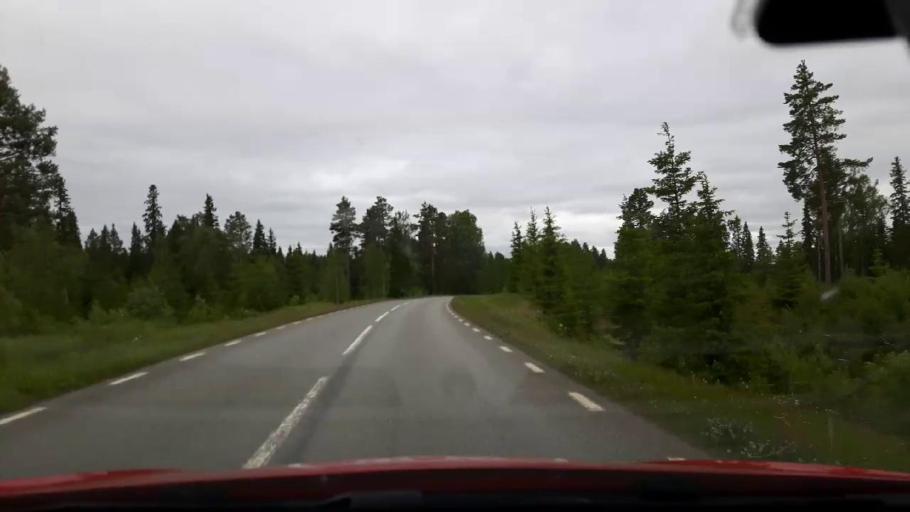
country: SE
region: Jaemtland
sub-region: Stroemsunds Kommun
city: Stroemsund
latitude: 63.4972
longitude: 15.4592
